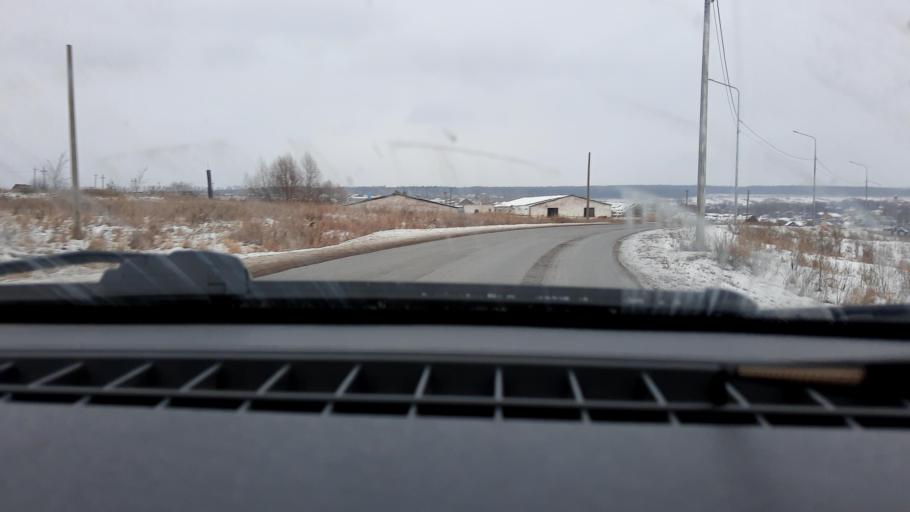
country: RU
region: Bashkortostan
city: Kabakovo
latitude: 54.7042
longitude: 56.2303
